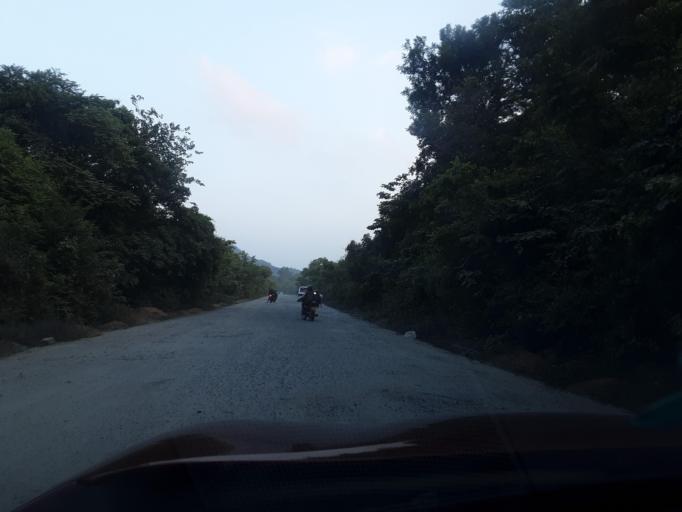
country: LK
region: Central
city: Dambulla
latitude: 7.8084
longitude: 80.7811
